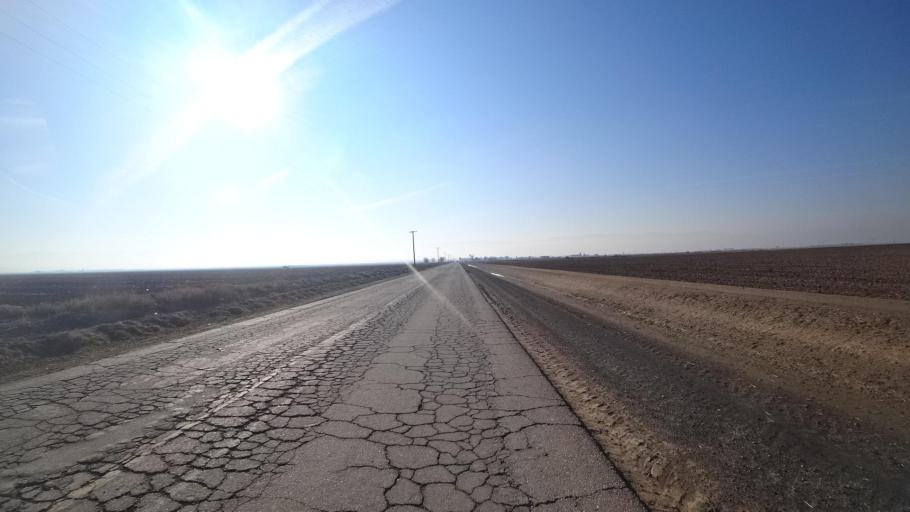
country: US
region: California
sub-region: Kern County
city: Weedpatch
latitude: 35.1762
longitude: -118.9678
